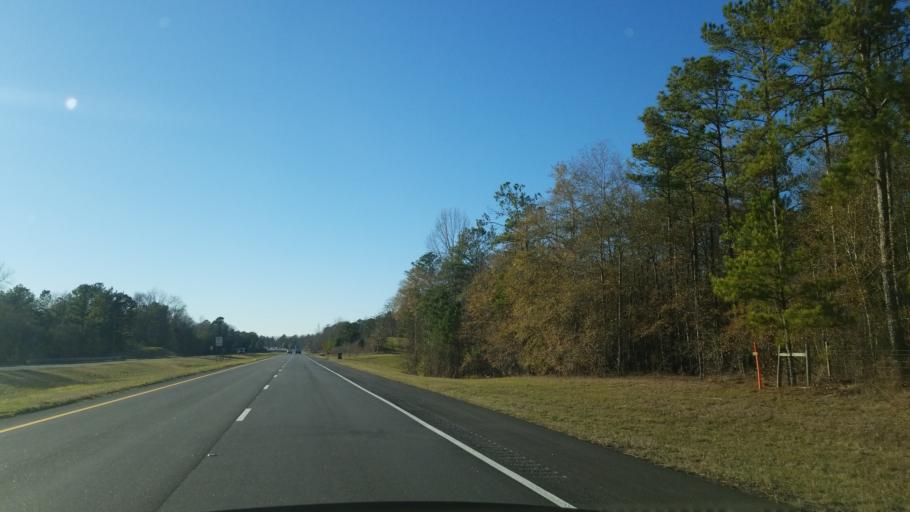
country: US
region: Georgia
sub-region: Talbot County
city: Talbotton
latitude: 32.5752
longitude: -84.5822
